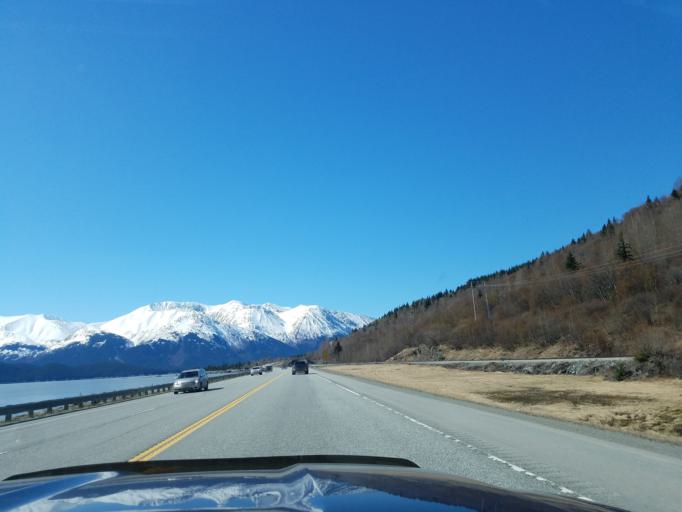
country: US
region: Alaska
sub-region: Anchorage Municipality
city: Girdwood
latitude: 60.9328
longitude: -149.3239
